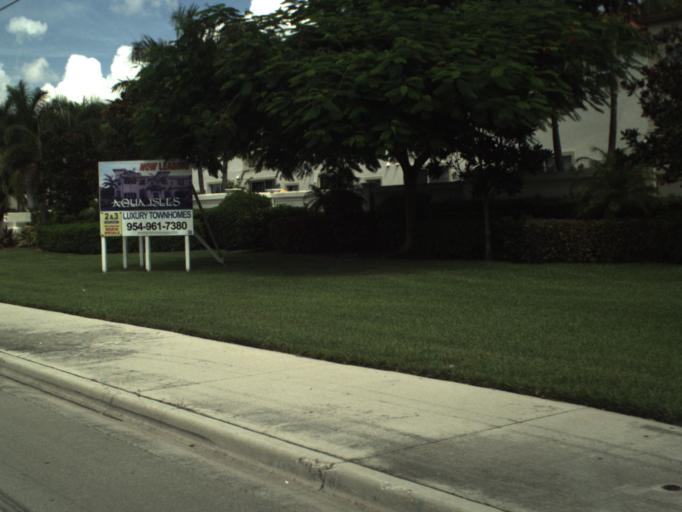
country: US
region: Florida
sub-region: Broward County
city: Davie
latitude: 26.0629
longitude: -80.1984
